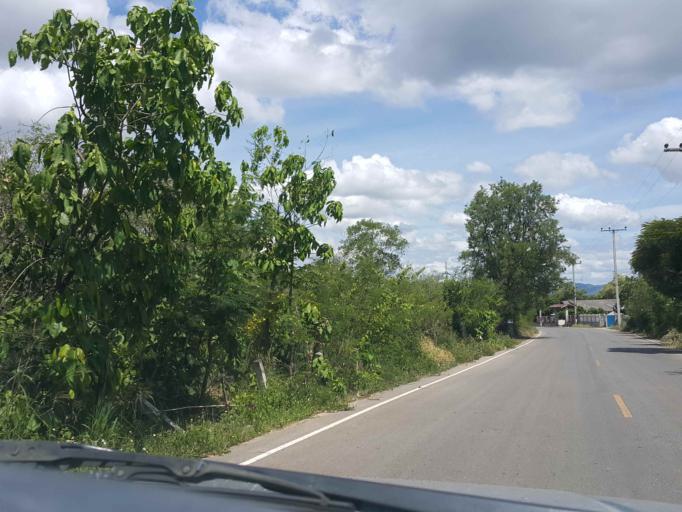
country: TH
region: Chiang Mai
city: Doi Lo
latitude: 18.4576
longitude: 98.7671
